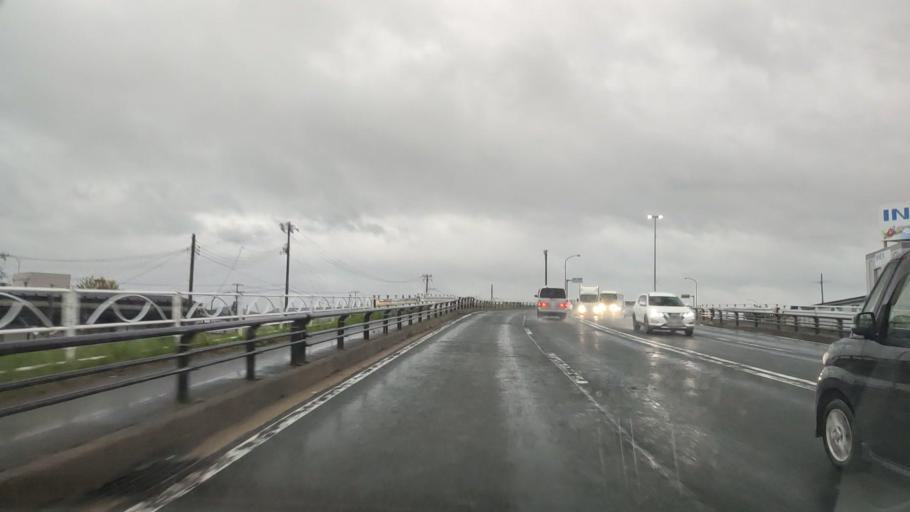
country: JP
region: Akita
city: Akita
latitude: 39.6981
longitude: 140.1170
